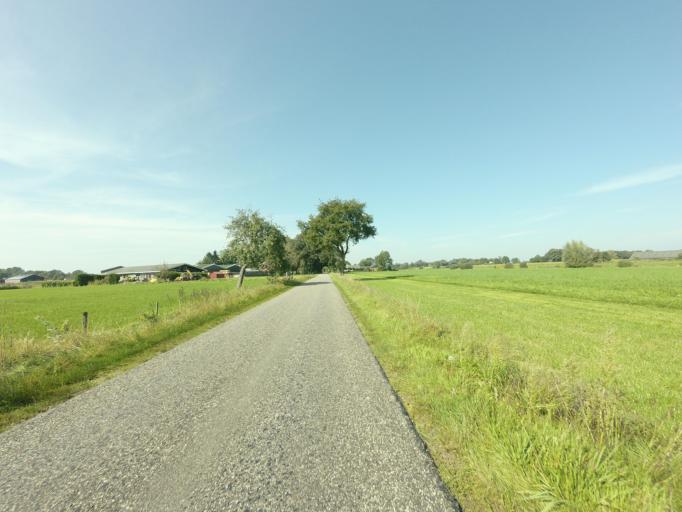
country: NL
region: Overijssel
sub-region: Gemeente Haaksbergen
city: Haaksbergen
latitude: 52.2100
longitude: 6.7617
